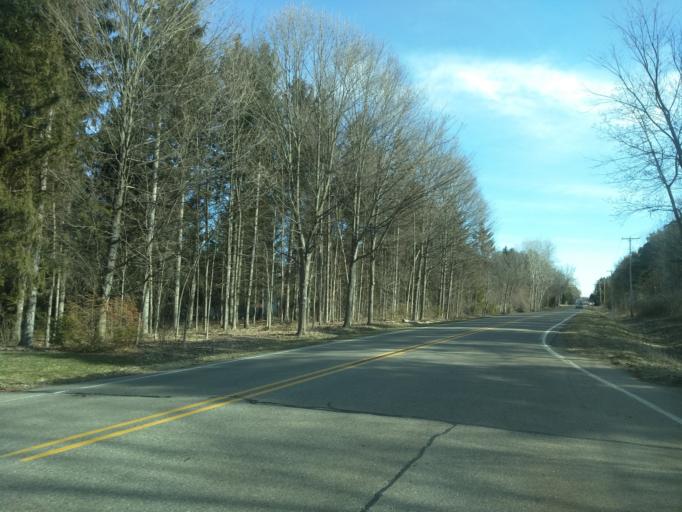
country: US
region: Michigan
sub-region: Clinton County
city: Bath
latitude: 42.7724
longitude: -84.4460
